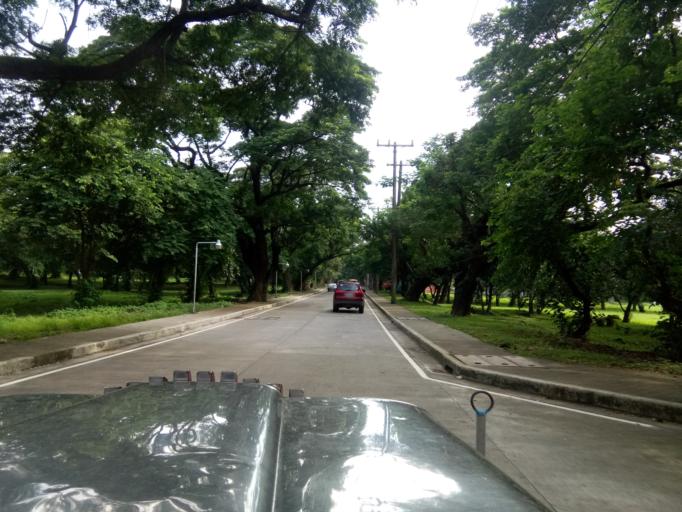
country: PH
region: Metro Manila
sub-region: Quezon City
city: Quezon City
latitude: 14.6545
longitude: 121.0623
